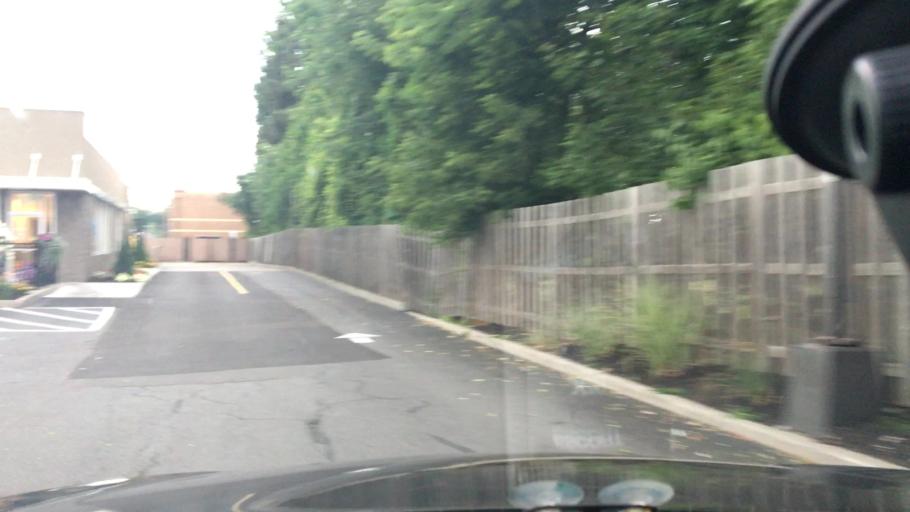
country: US
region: New York
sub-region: Erie County
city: West Seneca
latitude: 42.8317
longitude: -78.7543
